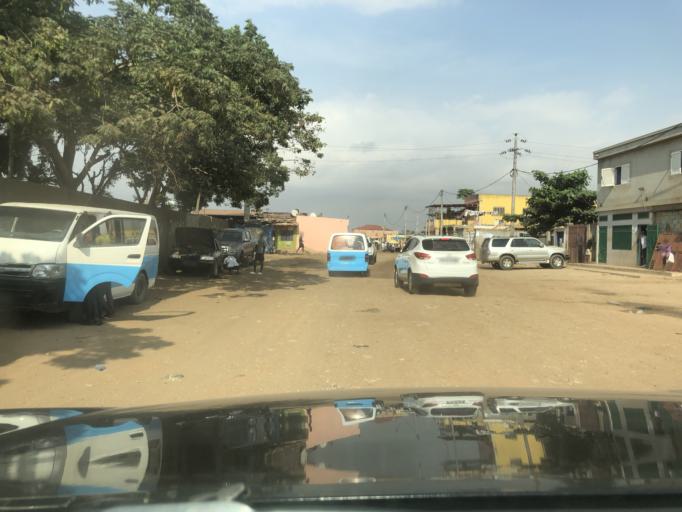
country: AO
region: Luanda
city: Luanda
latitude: -8.8564
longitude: 13.2546
